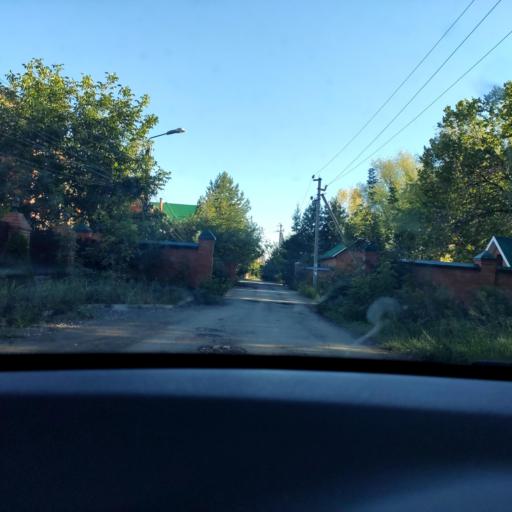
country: RU
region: Samara
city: Samara
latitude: 53.1549
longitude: 50.0821
